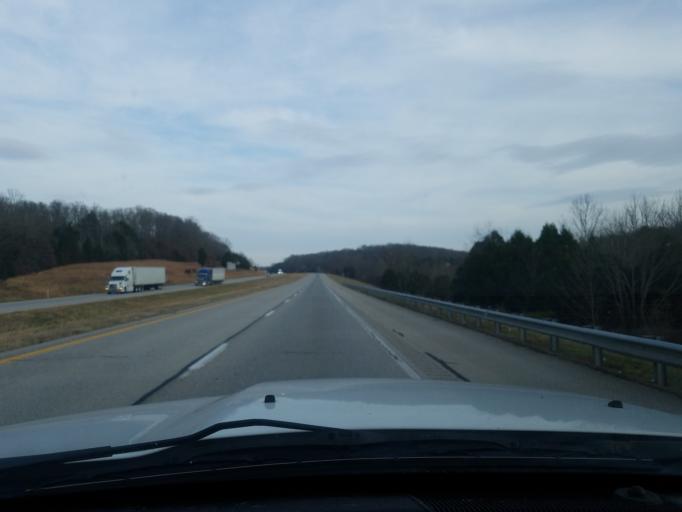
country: US
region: Indiana
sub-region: Crawford County
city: English
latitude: 38.2508
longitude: -86.3322
